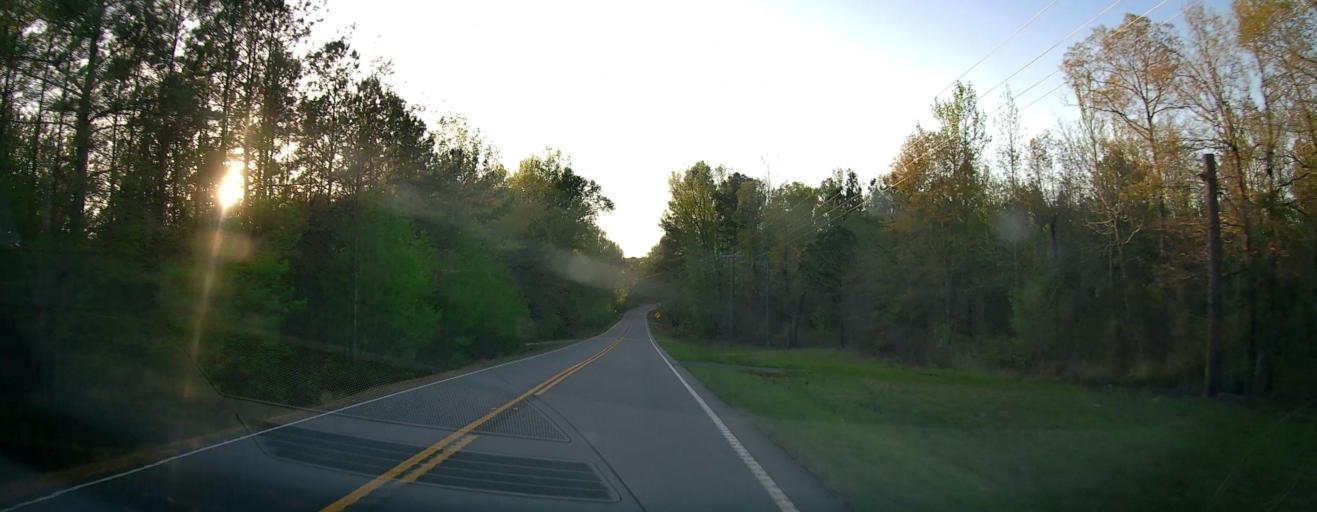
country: US
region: Georgia
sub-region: Talbot County
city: Talbotton
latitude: 32.5571
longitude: -84.5387
